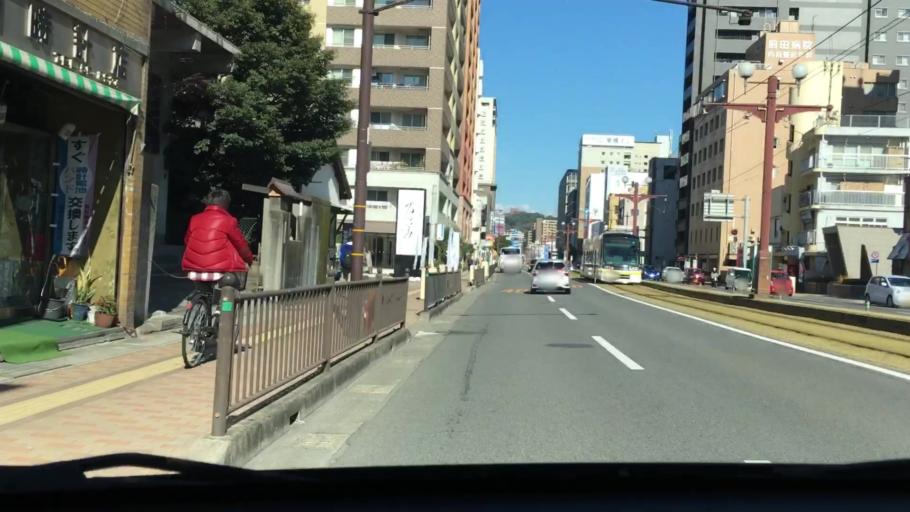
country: JP
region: Kagoshima
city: Kagoshima-shi
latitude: 31.5791
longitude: 130.5426
